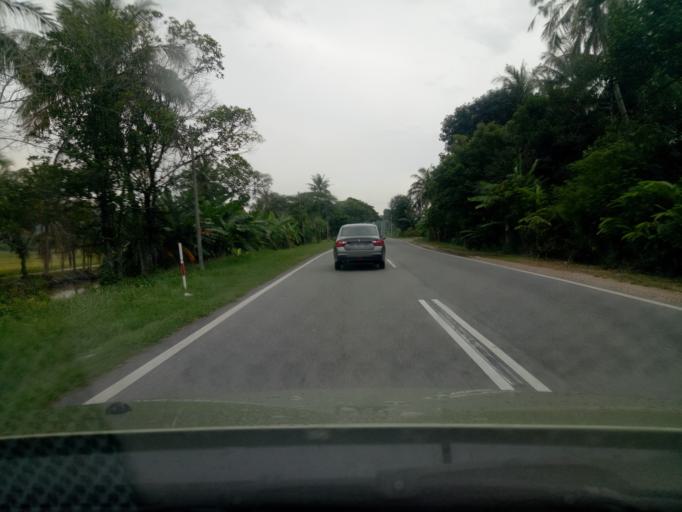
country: MY
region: Kedah
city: Gurun
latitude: 5.9688
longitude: 100.4274
